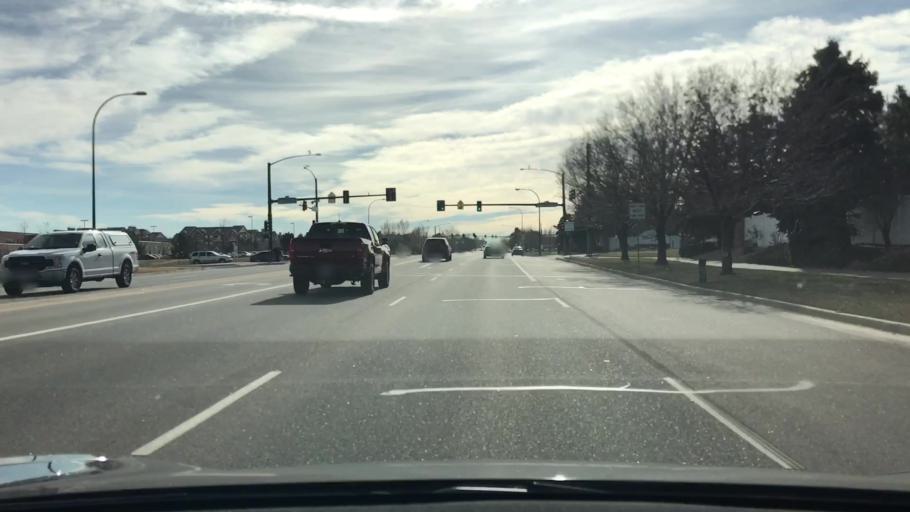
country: US
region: Colorado
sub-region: Adams County
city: Northglenn
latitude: 39.9248
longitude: -104.9969
